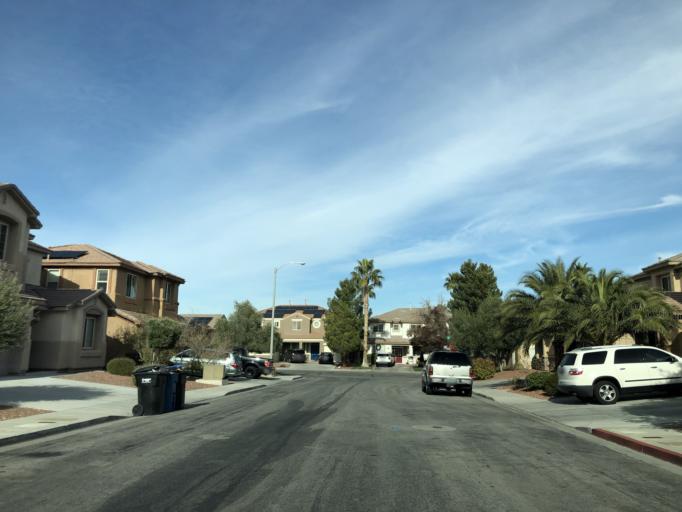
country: US
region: Nevada
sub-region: Clark County
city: Whitney
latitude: 36.0071
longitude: -115.0924
